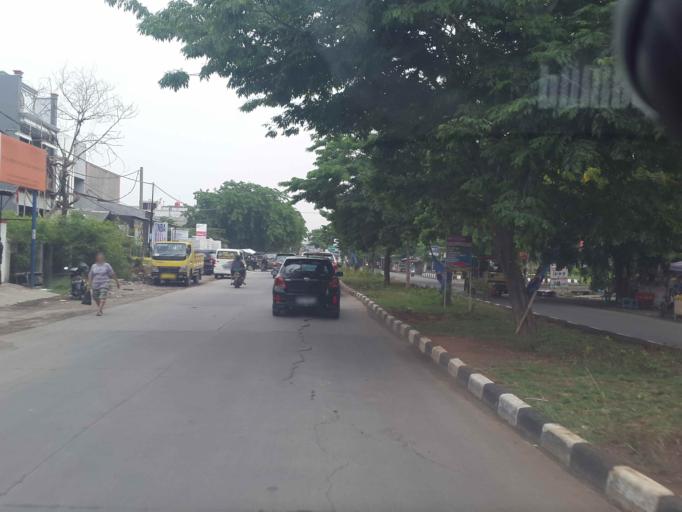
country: ID
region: West Java
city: Cikarang
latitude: -6.3320
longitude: 107.2843
